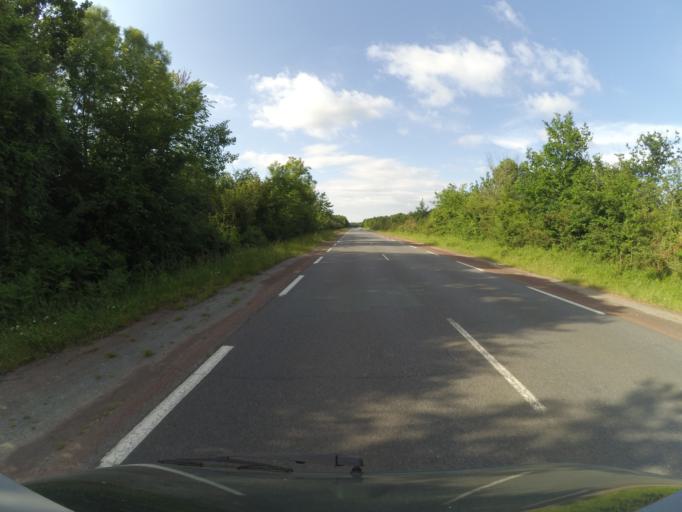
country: FR
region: Poitou-Charentes
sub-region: Departement de la Charente-Maritime
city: Le Gua
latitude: 45.7941
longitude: -0.9361
